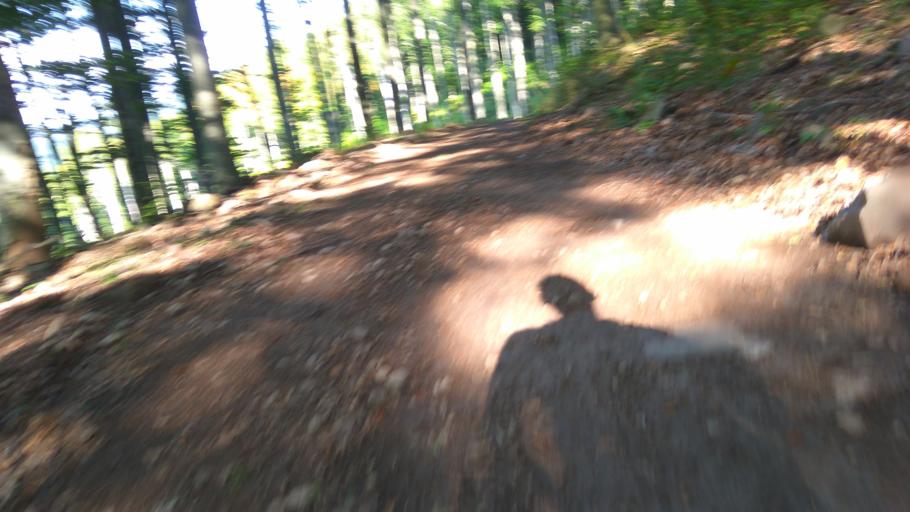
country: HU
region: Nograd
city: Diosjeno
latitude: 47.9772
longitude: 18.9605
